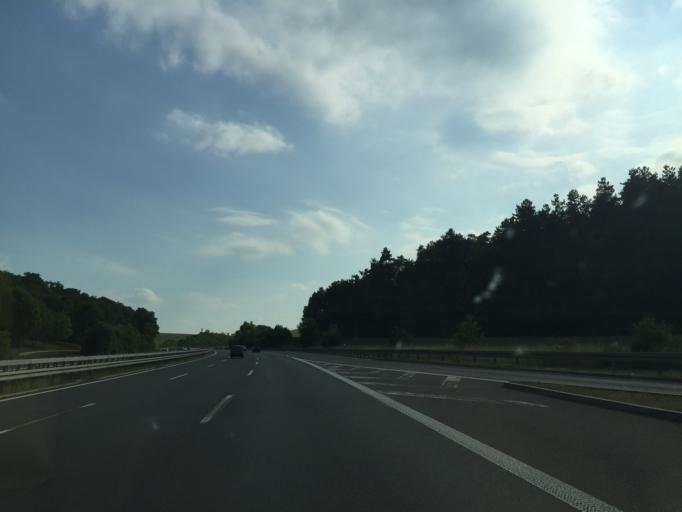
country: DE
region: Baden-Wuerttemberg
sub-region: Regierungsbezirk Stuttgart
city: Tauberbischofsheim
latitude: 49.5924
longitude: 9.6700
